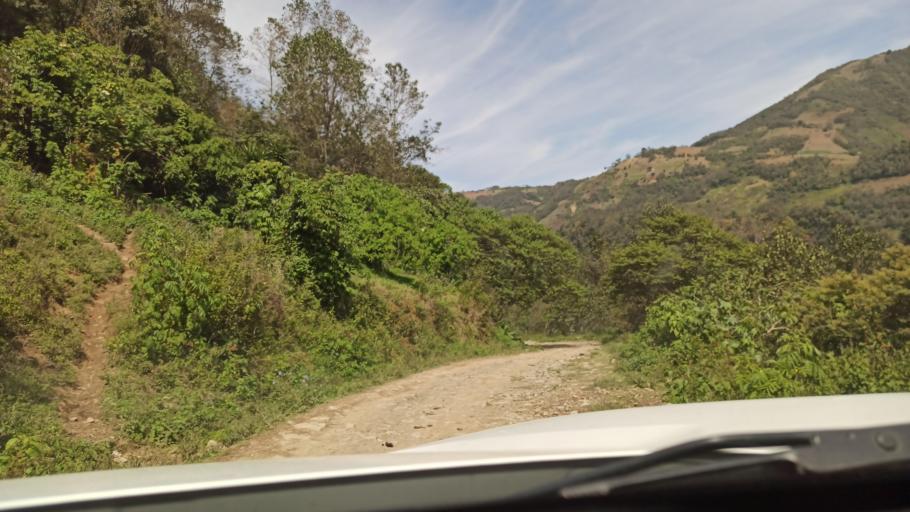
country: MX
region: Veracruz
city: Xocotla
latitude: 18.9803
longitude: -97.0971
